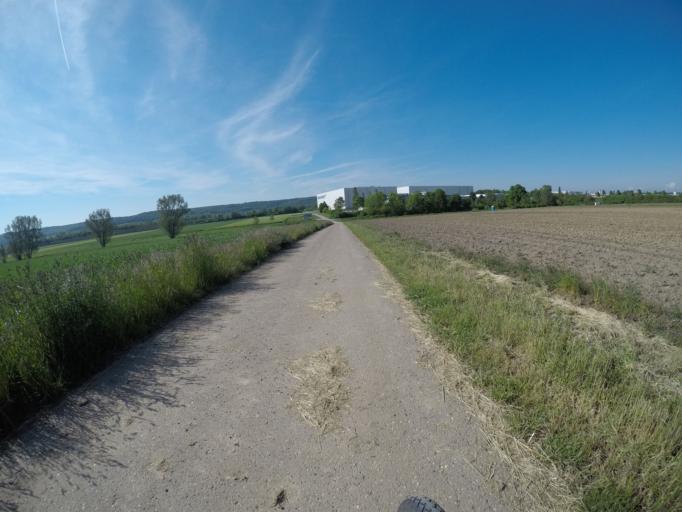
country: DE
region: Baden-Wuerttemberg
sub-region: Regierungsbezirk Stuttgart
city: Gartringen
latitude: 48.6419
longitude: 8.9207
